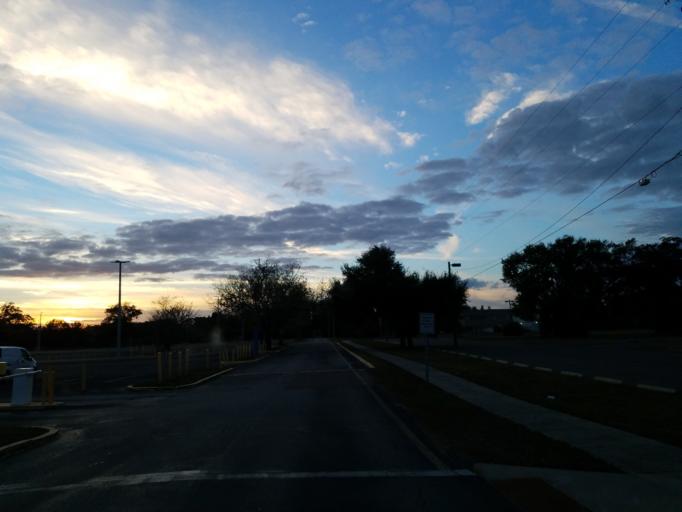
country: US
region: Florida
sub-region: Hillsborough County
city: Egypt Lake-Leto
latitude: 27.9773
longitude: -82.5102
